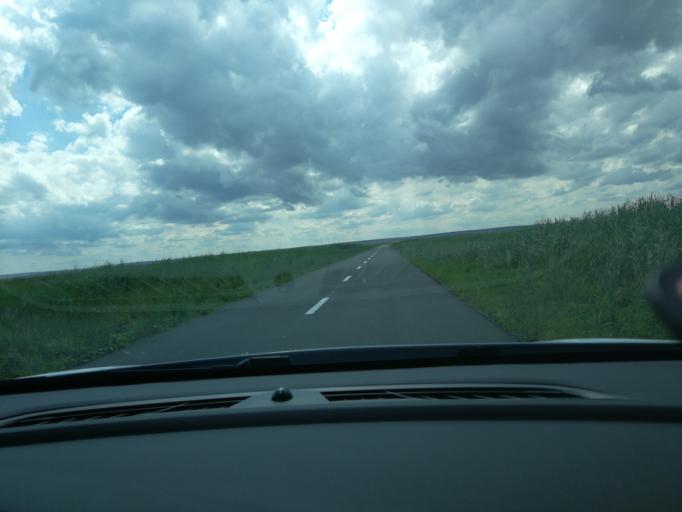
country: RO
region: Constanta
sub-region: Comuna Istria
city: Istria
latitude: 44.5369
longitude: 28.7425
